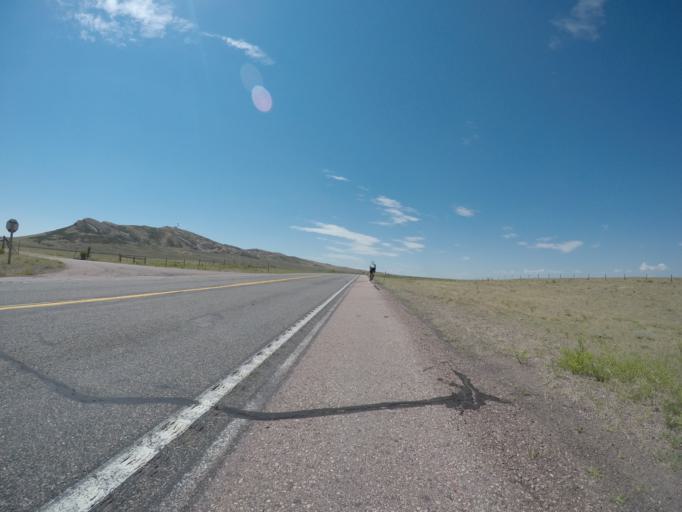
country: US
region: Wyoming
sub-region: Albany County
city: Laramie
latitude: 41.6584
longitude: -105.5342
